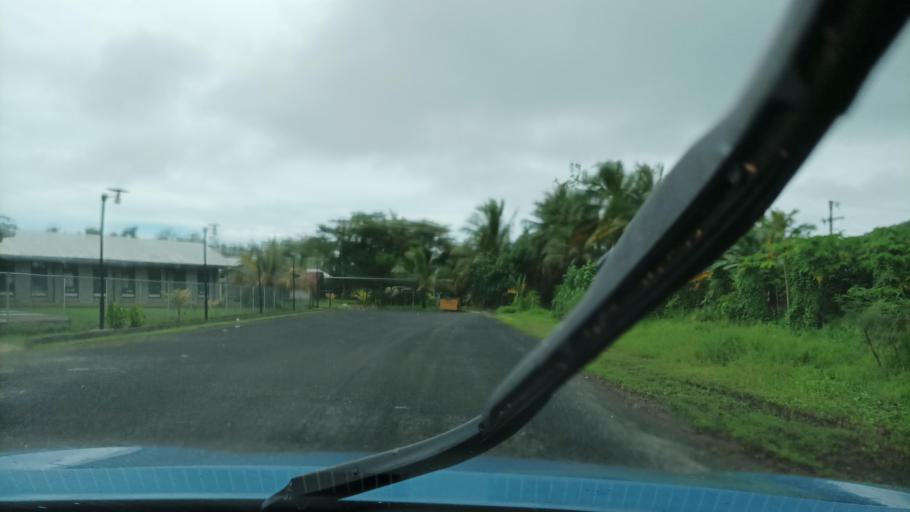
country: FM
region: Pohnpei
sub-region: Kolonia Municipality
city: Kolonia
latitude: 6.9545
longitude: 158.2208
